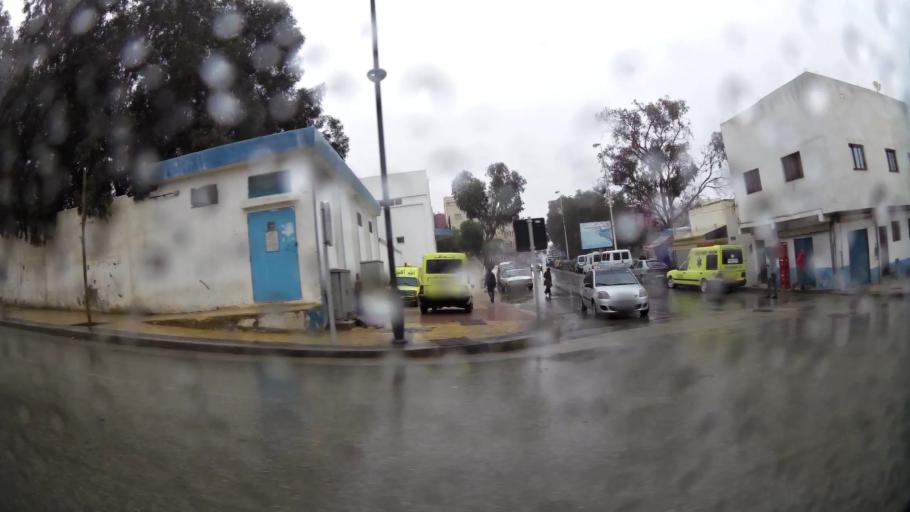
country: MA
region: Taza-Al Hoceima-Taounate
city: Al Hoceima
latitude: 35.2389
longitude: -3.9377
